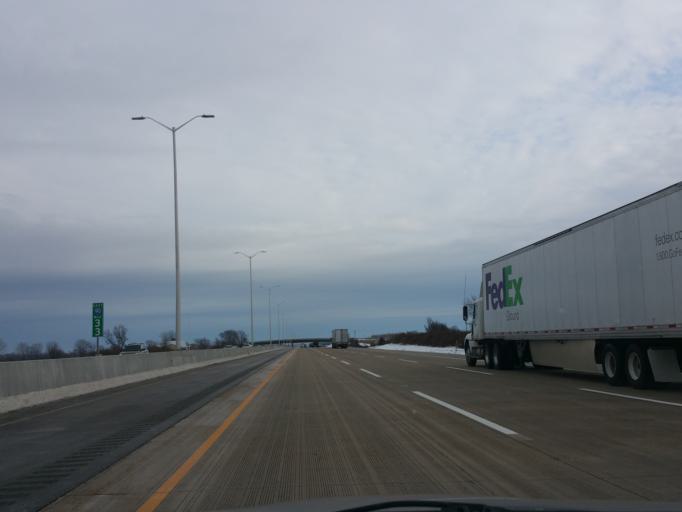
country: US
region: Illinois
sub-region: McHenry County
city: Marengo
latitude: 42.1969
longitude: -88.6735
